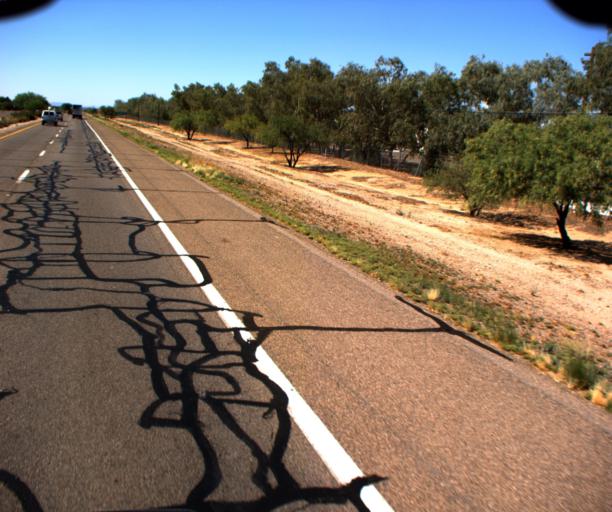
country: US
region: Arizona
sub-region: Pinal County
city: Casa Grande
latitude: 32.9575
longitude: -111.7569
